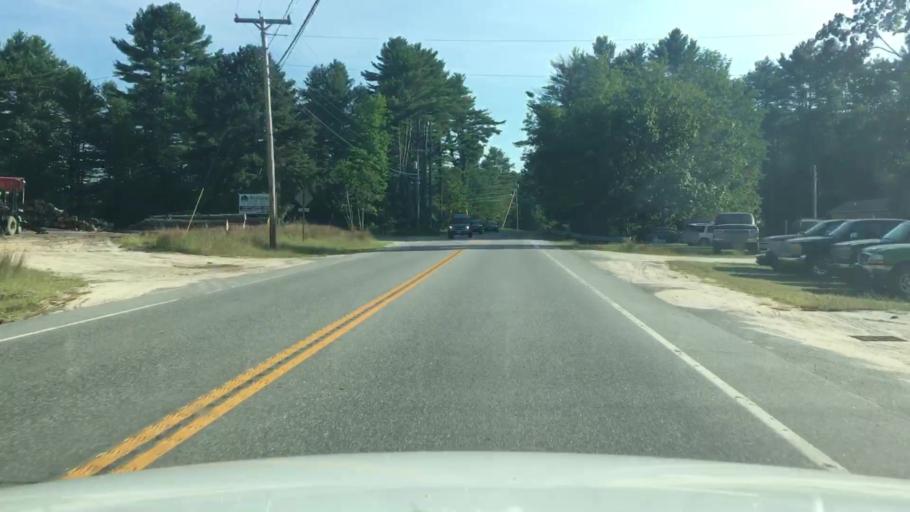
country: US
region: Maine
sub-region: Cumberland County
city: New Gloucester
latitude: 43.9272
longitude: -70.3104
